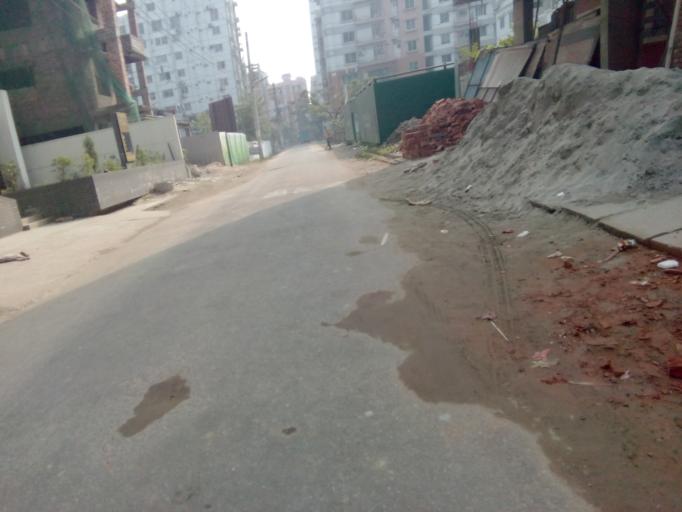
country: BD
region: Dhaka
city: Tungi
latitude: 23.8180
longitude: 90.4283
